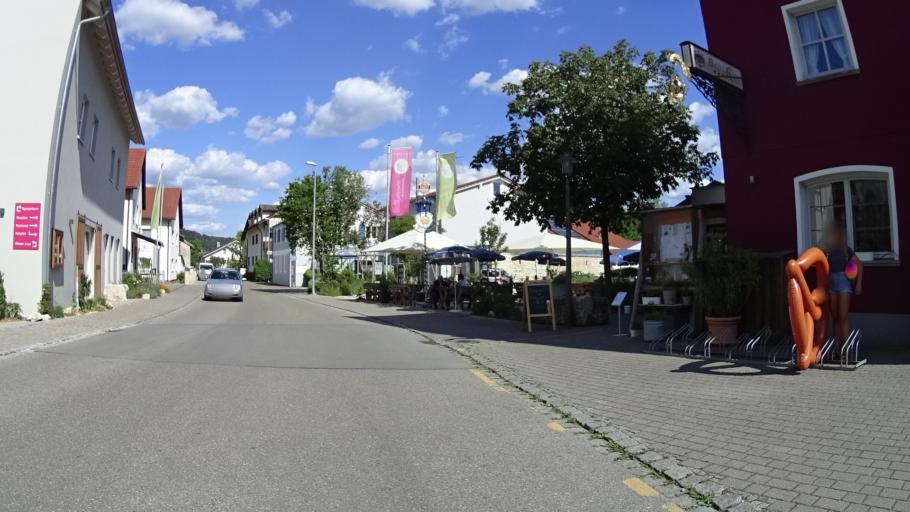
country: DE
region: Bavaria
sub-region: Regierungsbezirk Mittelfranken
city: Greding
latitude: 49.0005
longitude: 11.3835
